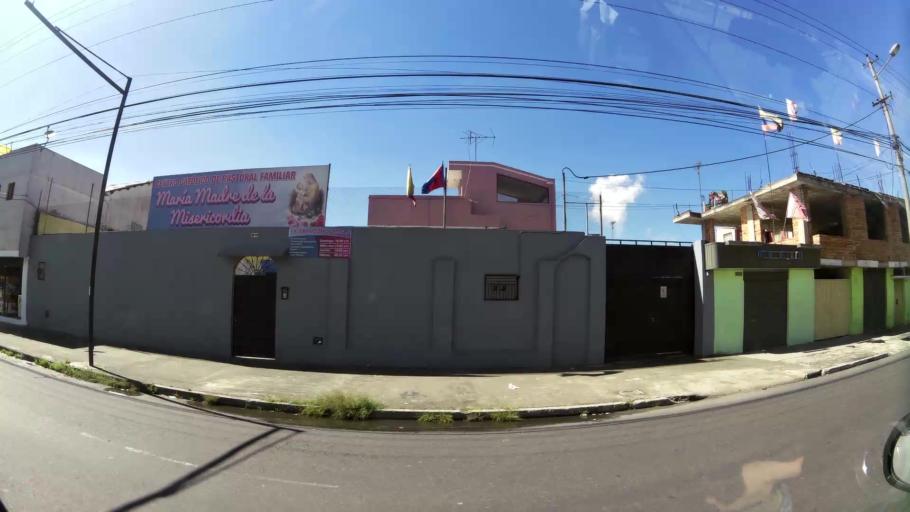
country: EC
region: Pichincha
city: Quito
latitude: -0.2400
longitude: -78.5241
